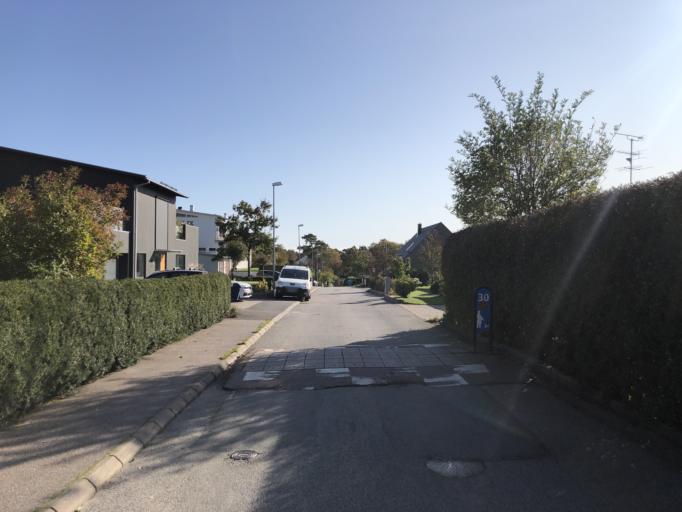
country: SE
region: Vaestra Goetaland
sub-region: Goteborg
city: Billdal
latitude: 57.6226
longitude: 11.8846
